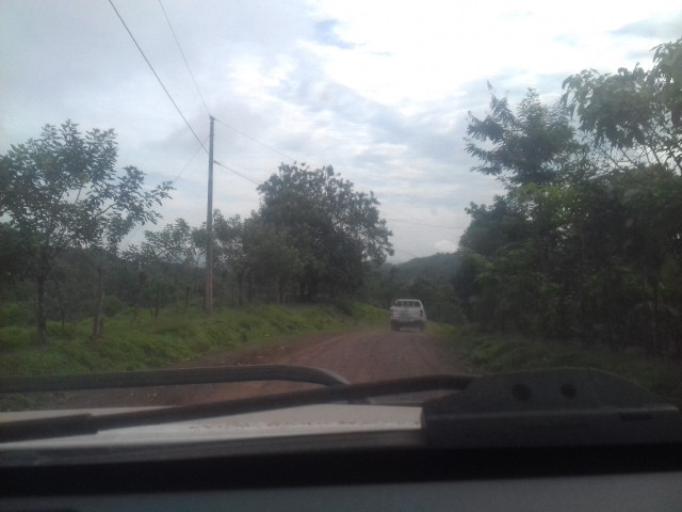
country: NI
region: Atlantico Norte (RAAN)
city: Waslala
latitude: 13.3922
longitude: -85.3274
